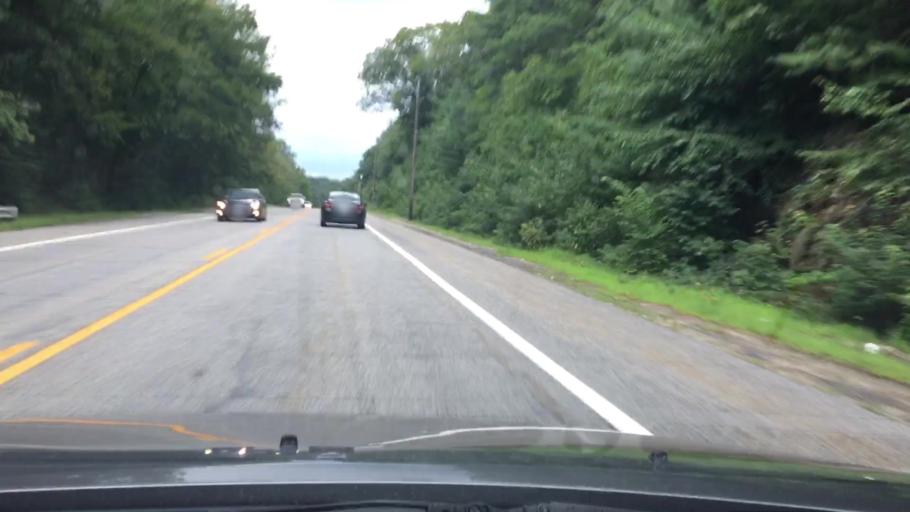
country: US
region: Rhode Island
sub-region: Providence County
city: Cumberland
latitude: 42.0079
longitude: -71.4251
